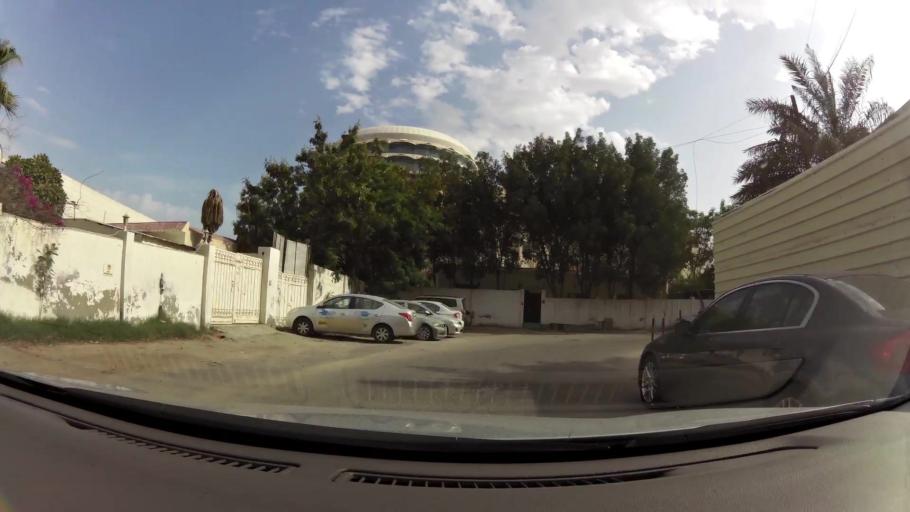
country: QA
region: Baladiyat ad Dawhah
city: Doha
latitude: 25.2753
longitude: 51.5122
